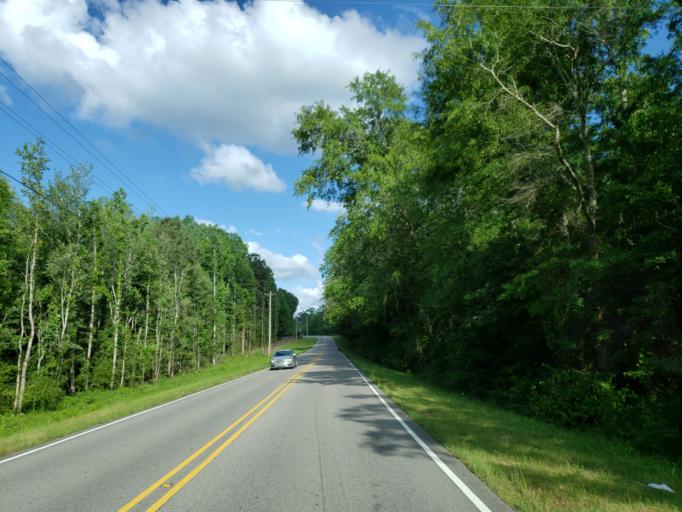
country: US
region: Mississippi
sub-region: Lamar County
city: West Hattiesburg
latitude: 31.2898
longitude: -89.4494
